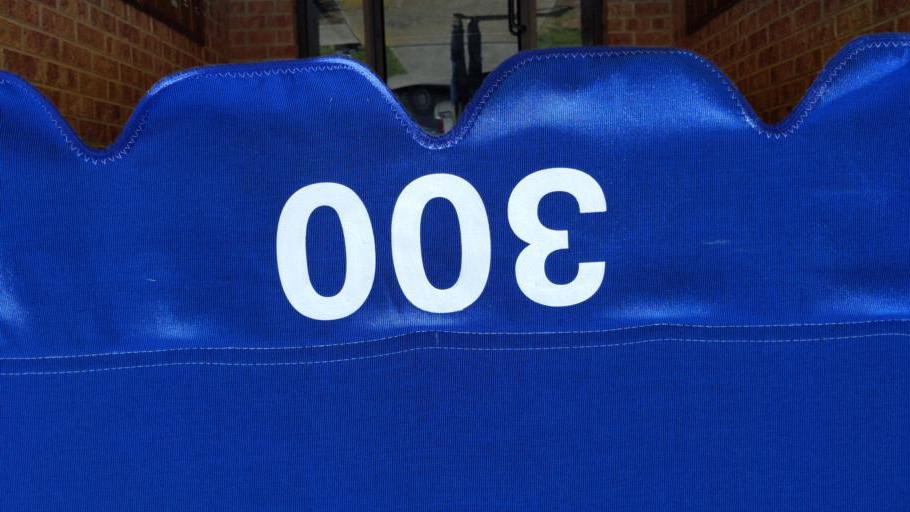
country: US
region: Virginia
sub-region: City of Radford
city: Radford
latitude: 37.1329
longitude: -80.5377
